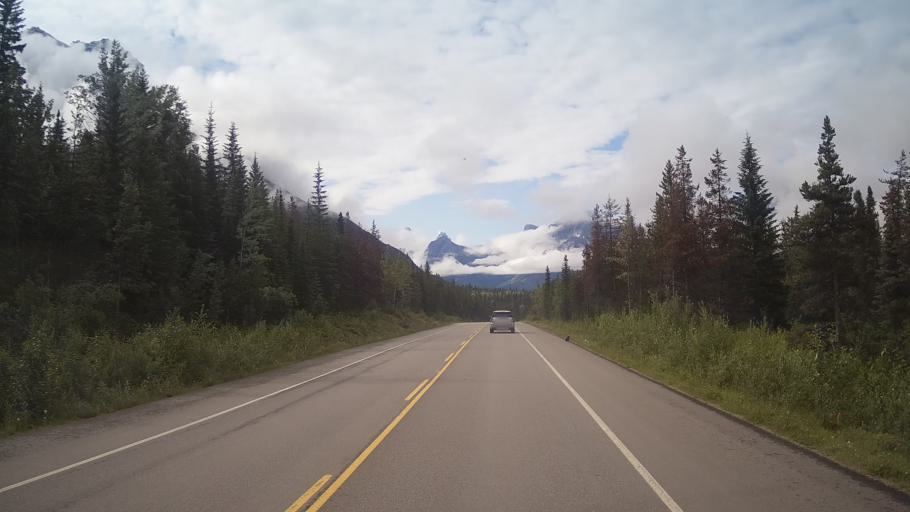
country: CA
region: Alberta
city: Jasper Park Lodge
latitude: 52.6890
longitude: -117.8657
